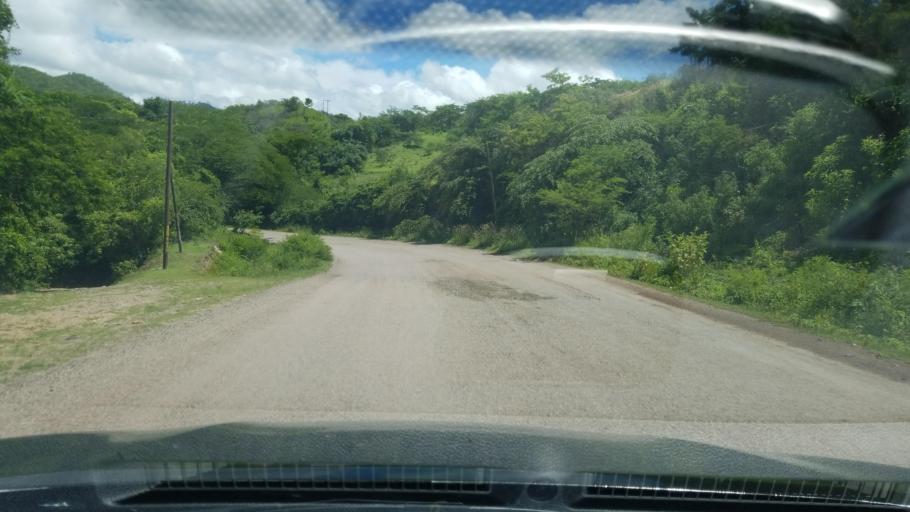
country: HN
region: Francisco Morazan
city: San Juan de Flores
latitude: 14.3145
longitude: -87.0391
